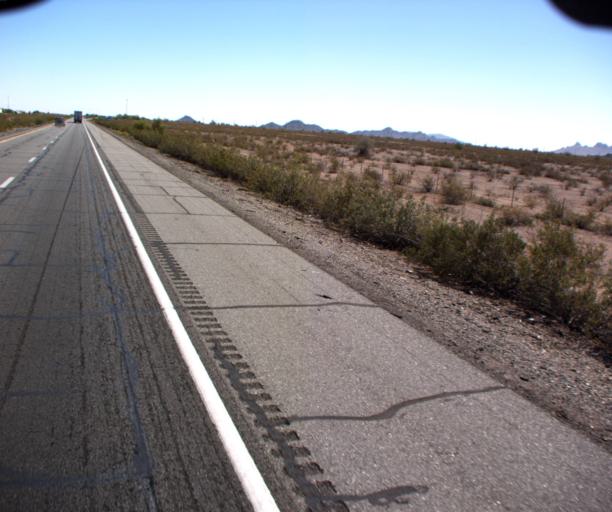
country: US
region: Arizona
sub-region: Maricopa County
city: Buckeye
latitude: 33.5221
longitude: -113.0807
